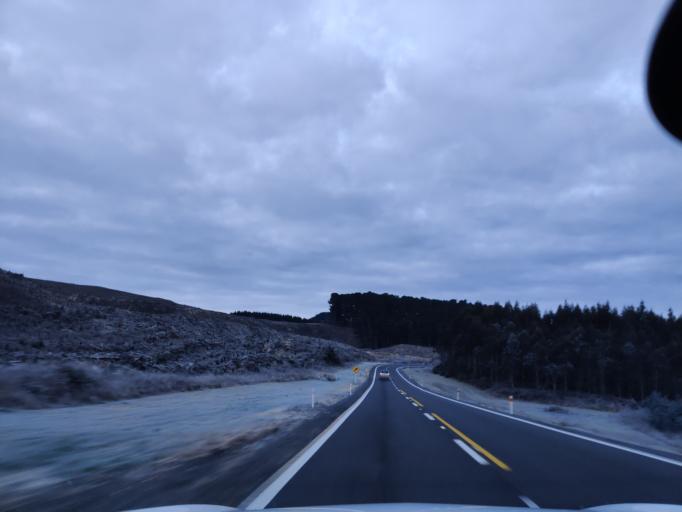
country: NZ
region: Waikato
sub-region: South Waikato District
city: Tokoroa
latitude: -38.4075
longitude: 176.0514
